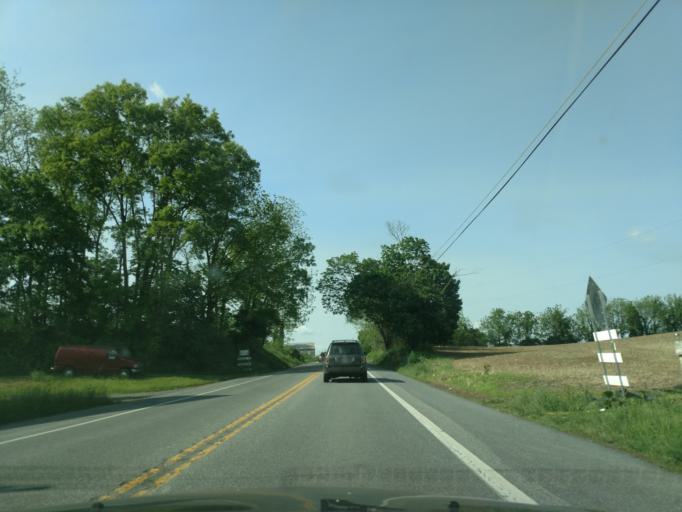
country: US
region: Pennsylvania
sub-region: Lebanon County
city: Cornwall
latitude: 40.2999
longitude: -76.4244
